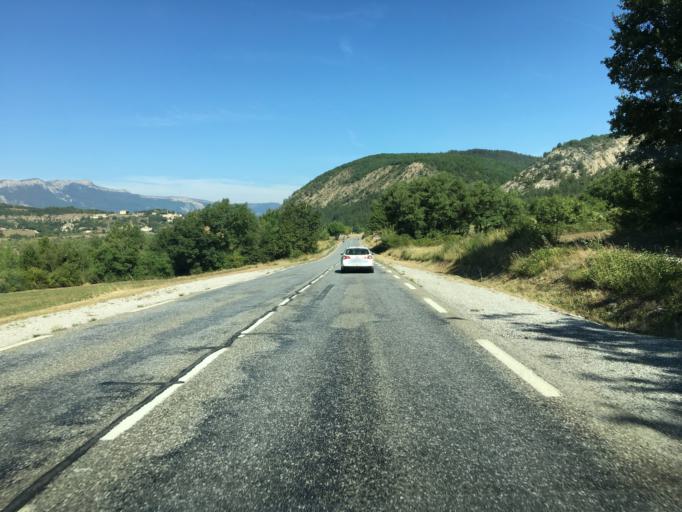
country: FR
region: Provence-Alpes-Cote d'Azur
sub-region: Departement des Hautes-Alpes
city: Laragne-Monteglin
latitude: 44.3281
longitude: 5.7913
